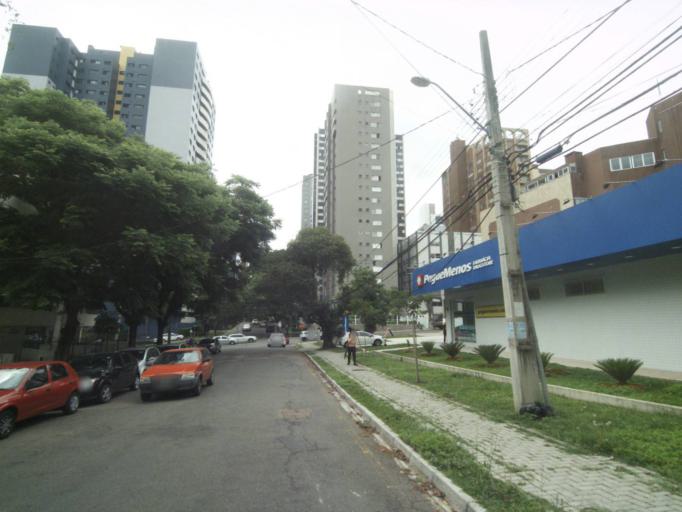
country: BR
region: Parana
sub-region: Curitiba
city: Curitiba
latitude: -25.4351
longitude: -49.3003
